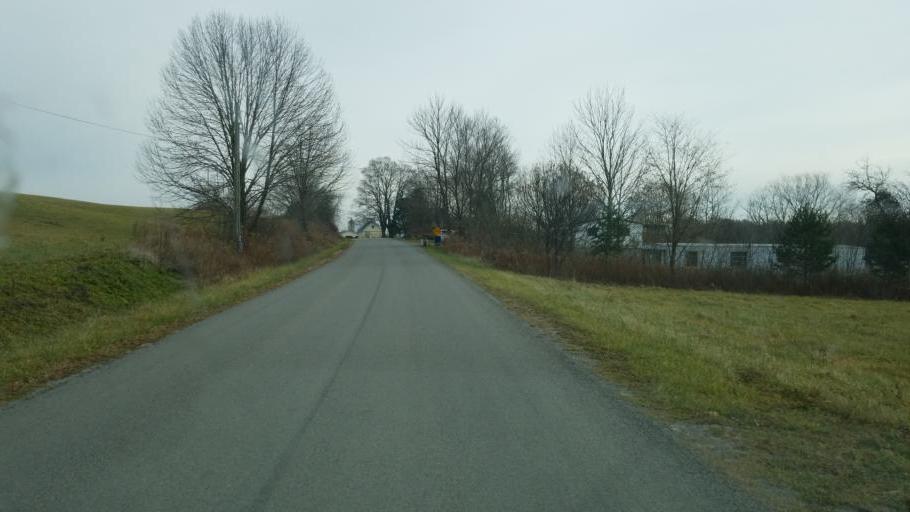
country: US
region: Pennsylvania
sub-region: Crawford County
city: Cochranton
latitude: 41.5060
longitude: -80.0931
